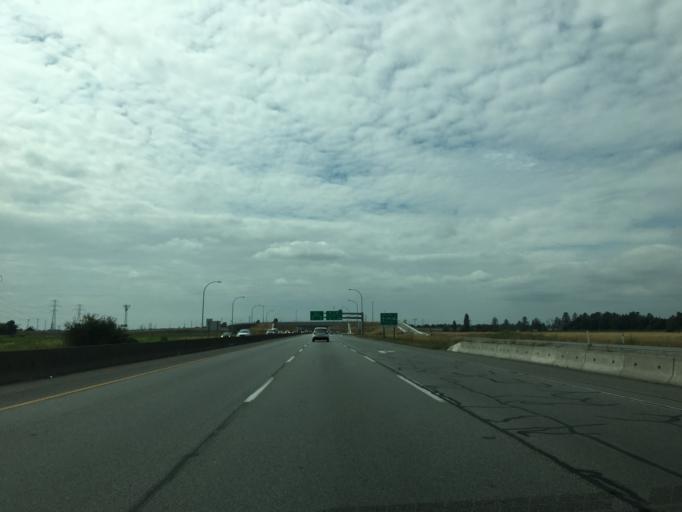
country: CA
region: British Columbia
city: Ladner
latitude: 49.0929
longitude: -123.0137
